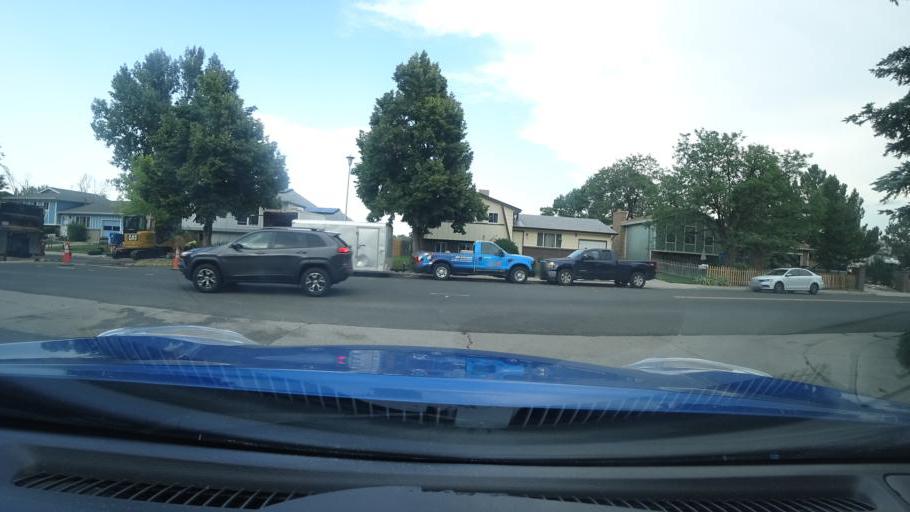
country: US
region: Colorado
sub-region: Adams County
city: Aurora
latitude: 39.6879
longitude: -104.8071
